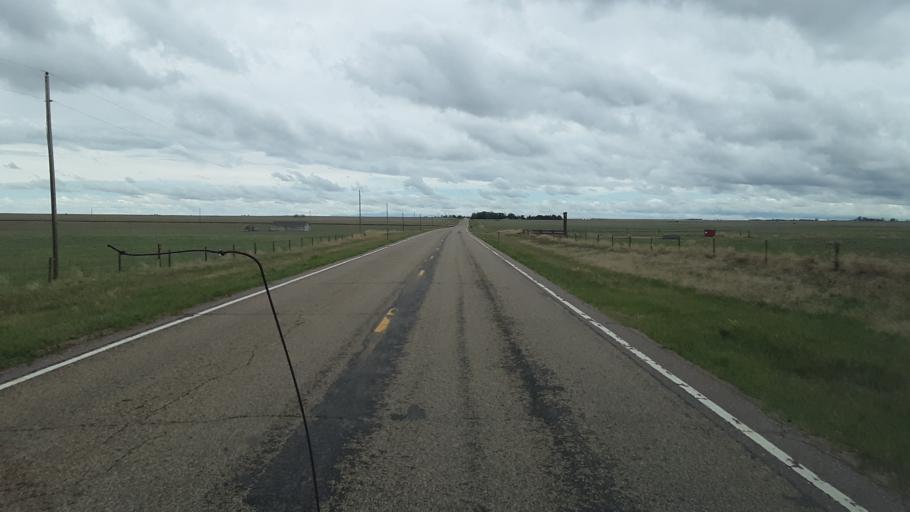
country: US
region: Colorado
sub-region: El Paso County
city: Ellicott
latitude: 38.8397
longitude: -104.0338
